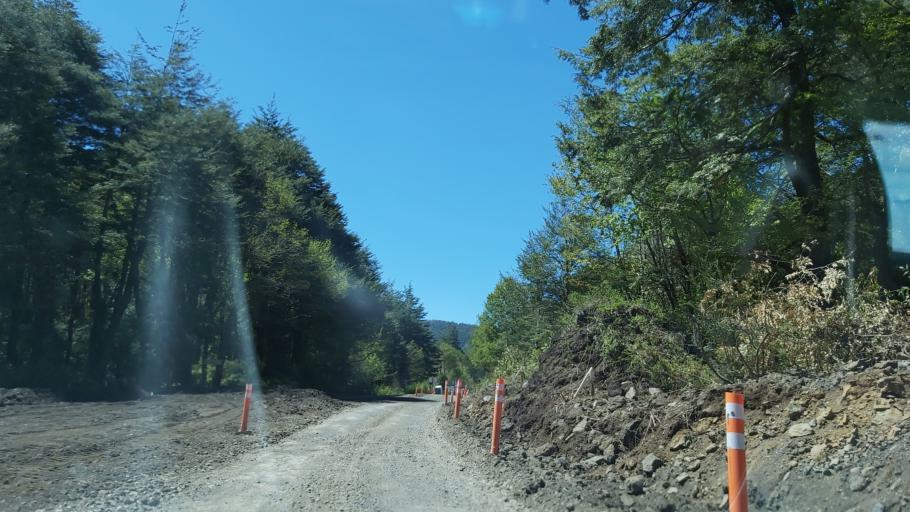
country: CL
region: Araucania
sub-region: Provincia de Cautin
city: Vilcun
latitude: -38.4705
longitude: -71.6754
